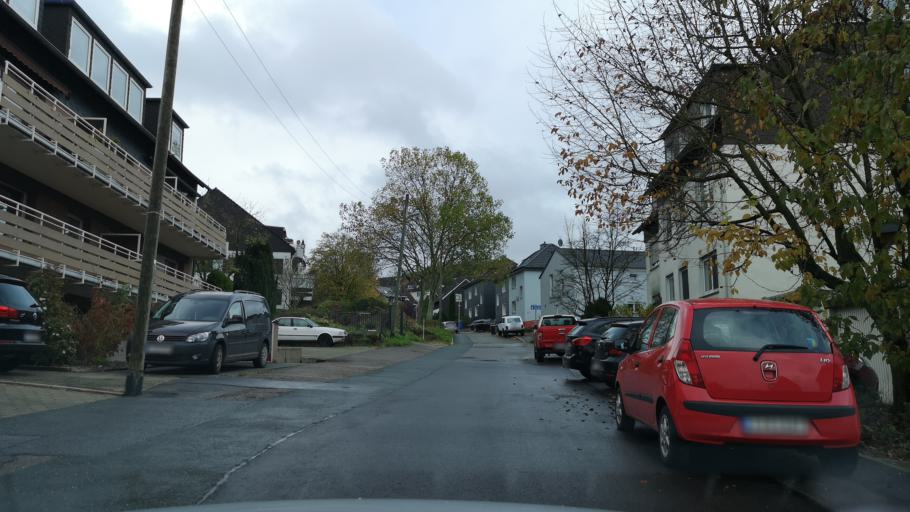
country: DE
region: North Rhine-Westphalia
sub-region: Regierungsbezirk Dusseldorf
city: Velbert
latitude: 51.4014
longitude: 7.0931
